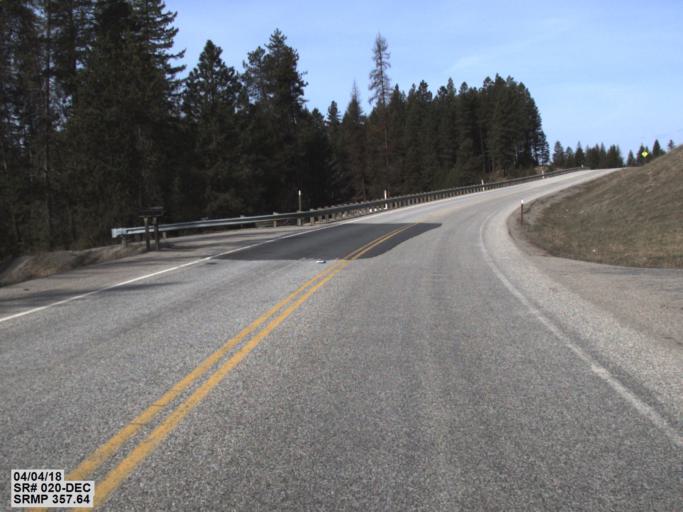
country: US
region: Washington
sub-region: Stevens County
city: Colville
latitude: 48.5403
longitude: -117.8380
